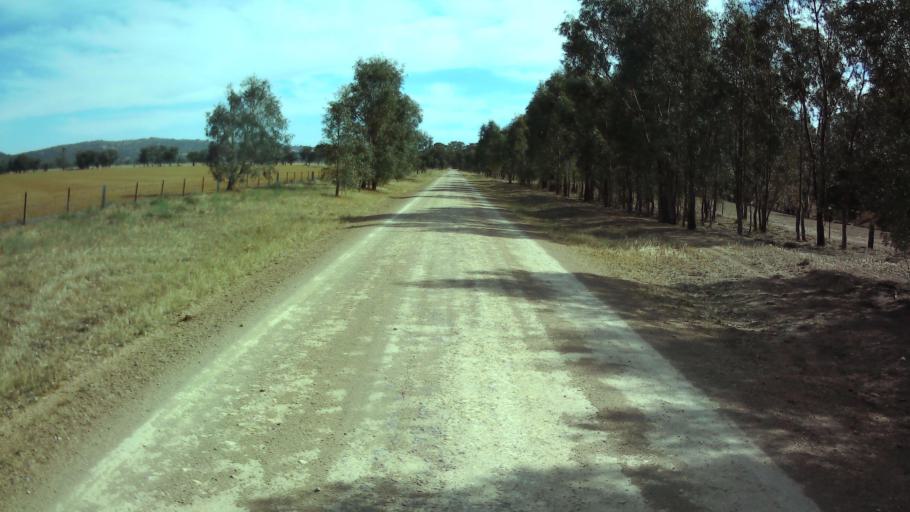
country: AU
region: New South Wales
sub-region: Weddin
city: Grenfell
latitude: -33.7073
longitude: 148.3010
